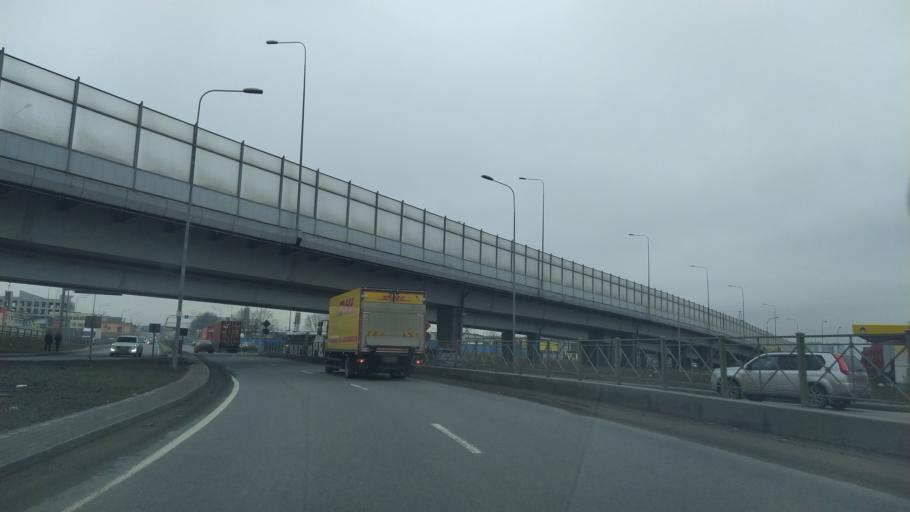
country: RU
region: St.-Petersburg
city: Kupchino
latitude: 59.8323
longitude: 30.3108
